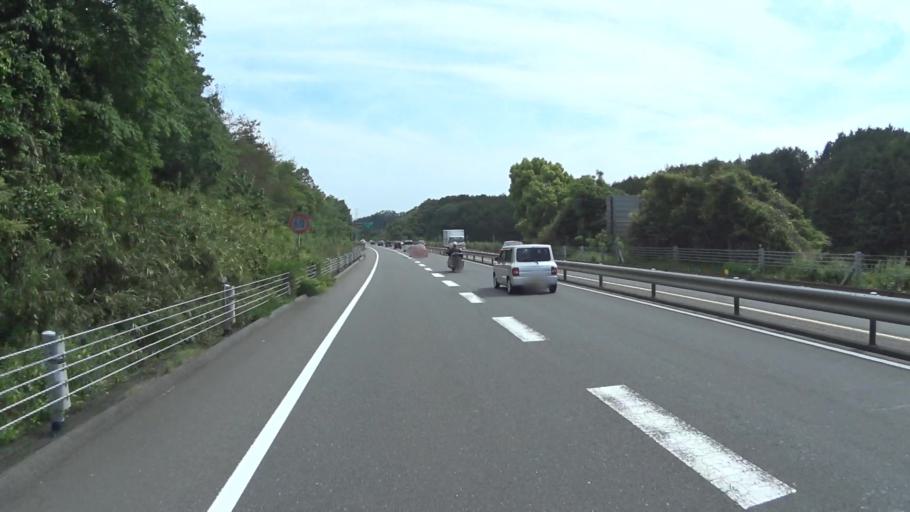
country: JP
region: Shiga Prefecture
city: Kitahama
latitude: 35.1232
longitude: 135.8991
